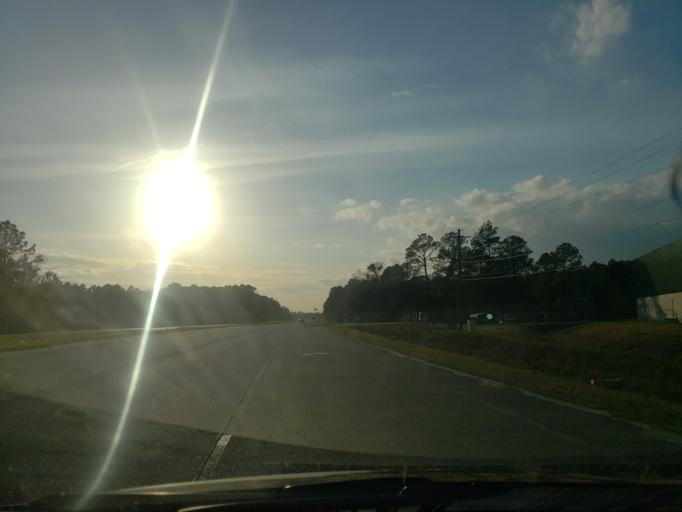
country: US
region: Georgia
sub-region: Chatham County
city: Bloomingdale
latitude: 32.1492
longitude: -81.2868
